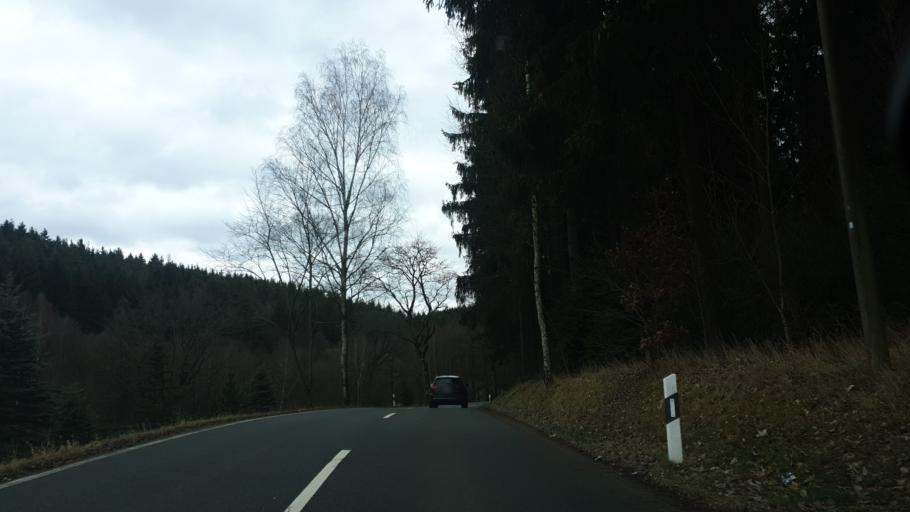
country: DE
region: Saxony
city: Markneukirchen
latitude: 50.2765
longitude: 12.2903
